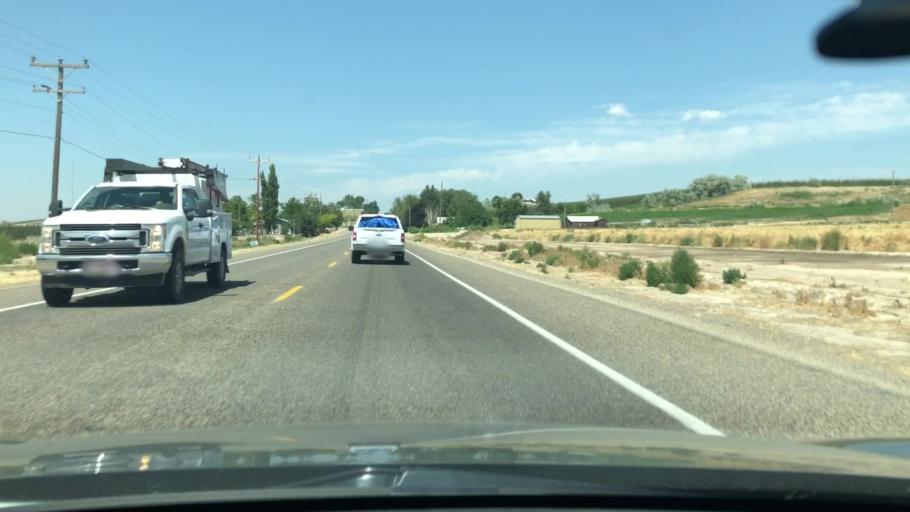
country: US
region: Idaho
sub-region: Canyon County
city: Wilder
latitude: 43.6518
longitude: -116.9119
